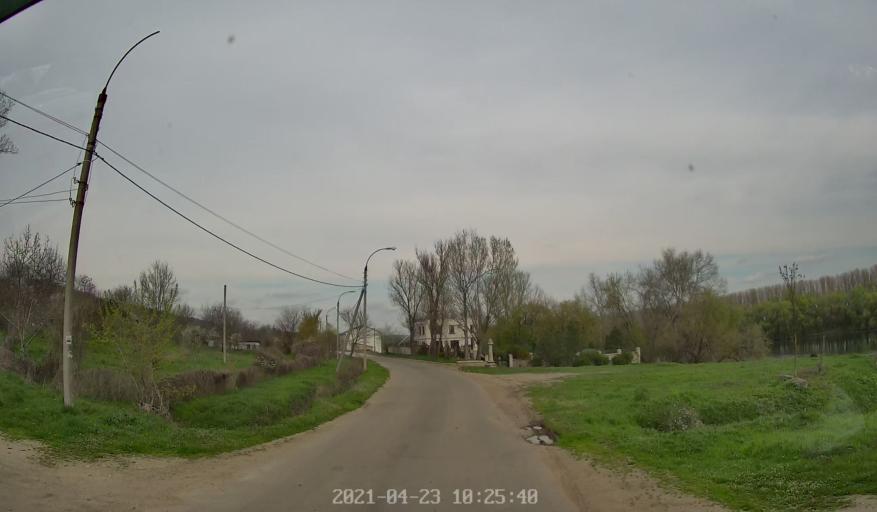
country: MD
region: Chisinau
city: Vadul lui Voda
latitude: 47.0921
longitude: 29.0804
